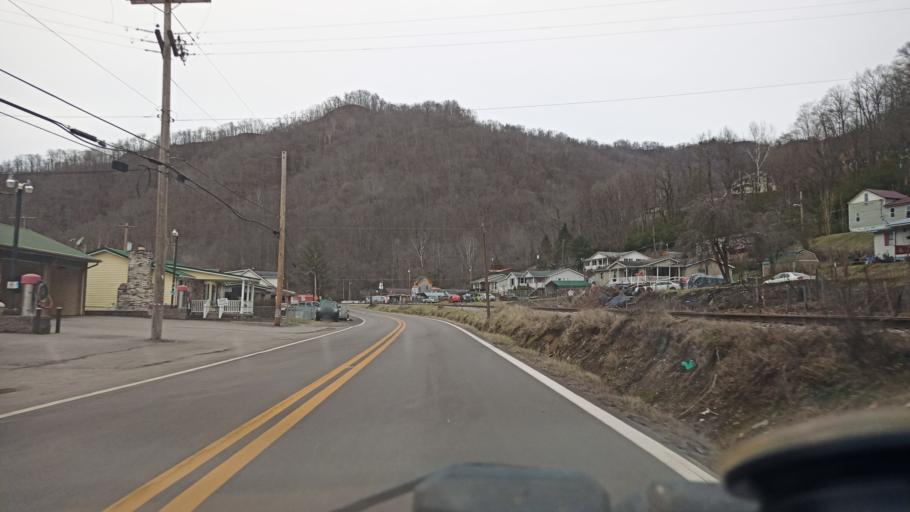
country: US
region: West Virginia
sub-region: Logan County
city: Mallory
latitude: 37.6899
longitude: -81.8543
